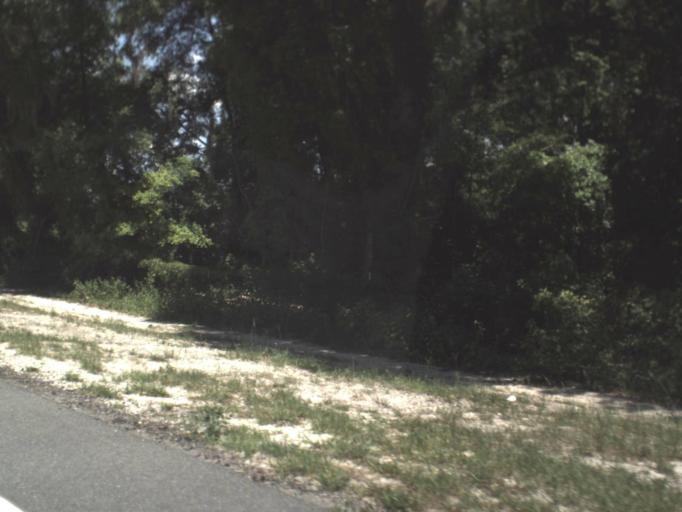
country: US
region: Florida
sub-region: Dixie County
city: Cross City
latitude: 29.7518
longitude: -82.9840
